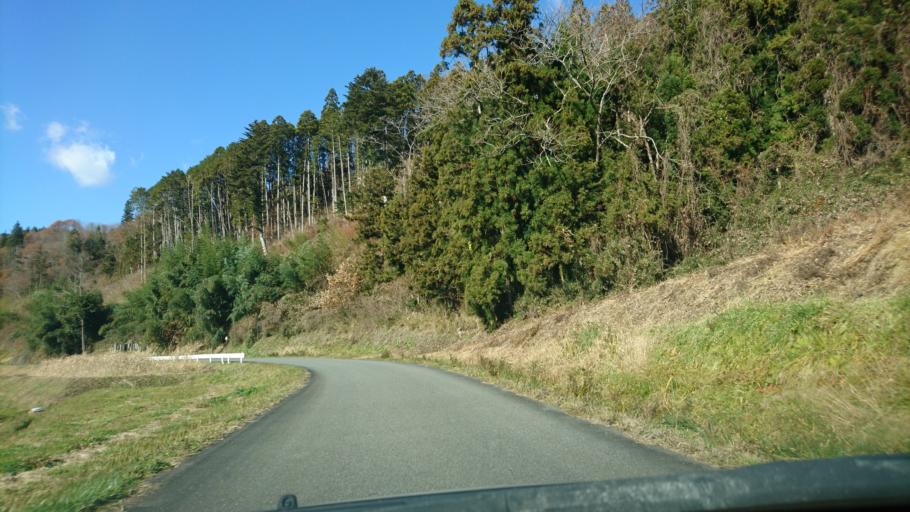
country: JP
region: Iwate
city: Ichinoseki
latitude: 39.0015
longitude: 141.0778
